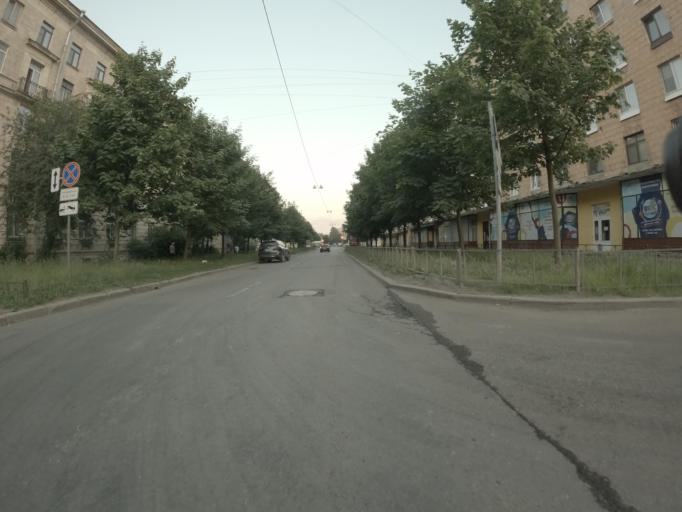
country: RU
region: St.-Petersburg
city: Centralniy
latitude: 59.9291
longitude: 30.4062
